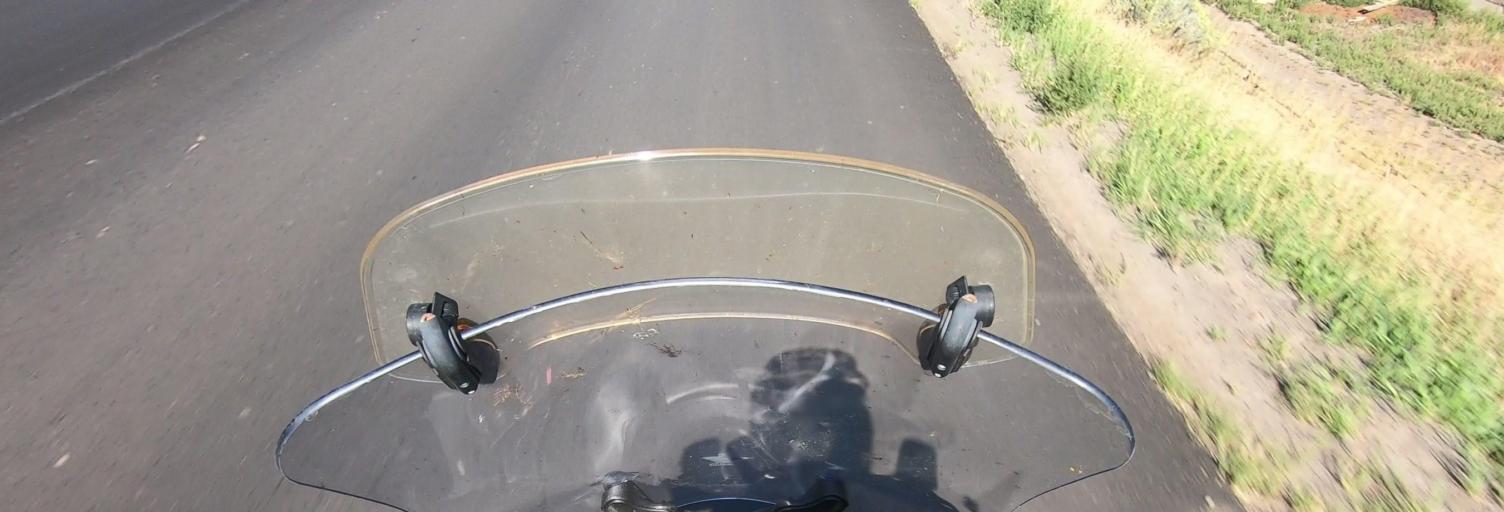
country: CA
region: British Columbia
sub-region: Thompson-Nicola Regional District
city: Ashcroft
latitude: 50.7904
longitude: -121.2366
